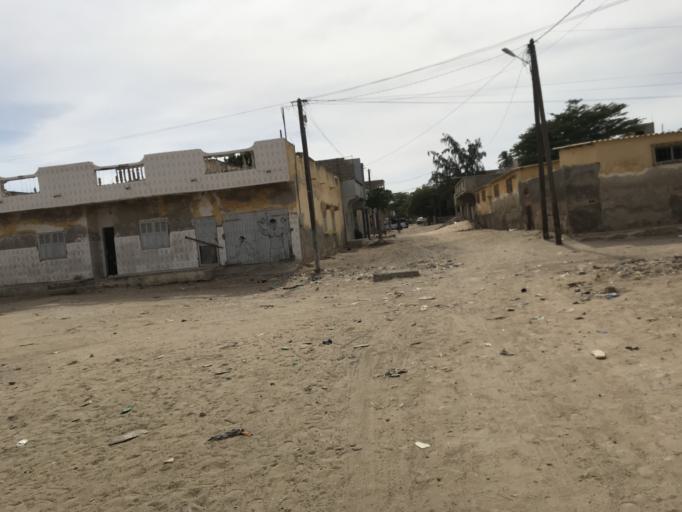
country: SN
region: Saint-Louis
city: Saint-Louis
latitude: 16.0247
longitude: -16.4847
